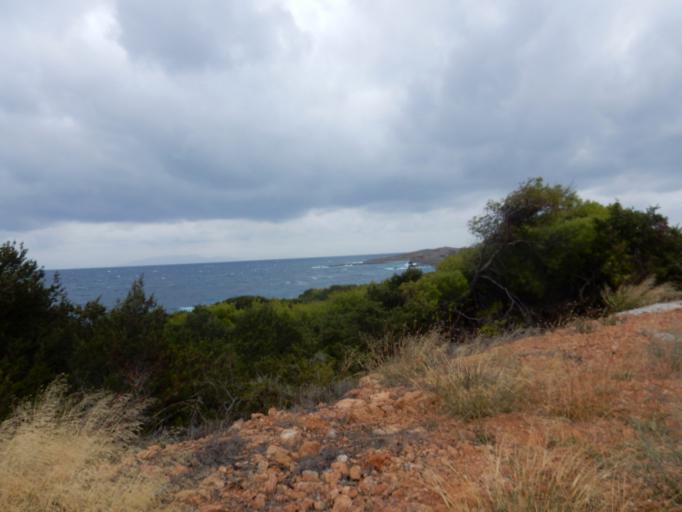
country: GR
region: Attica
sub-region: Nomarchia Anatolikis Attikis
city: Limin Mesoyaias
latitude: 37.9190
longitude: 24.0304
